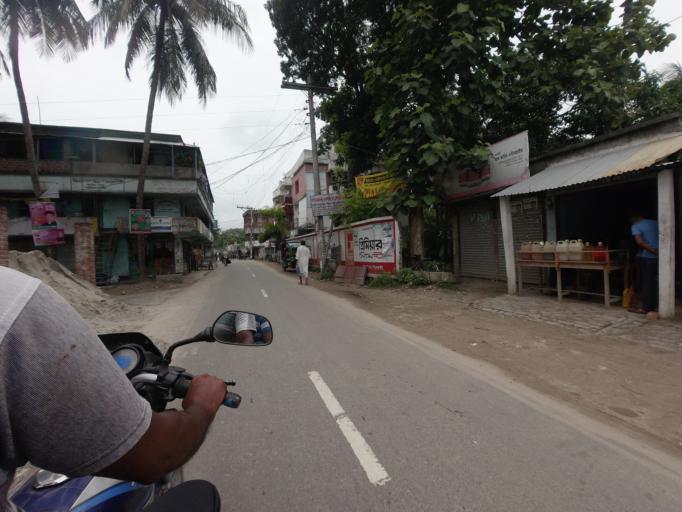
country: BD
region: Khulna
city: Kalia
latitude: 23.1798
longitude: 89.6477
